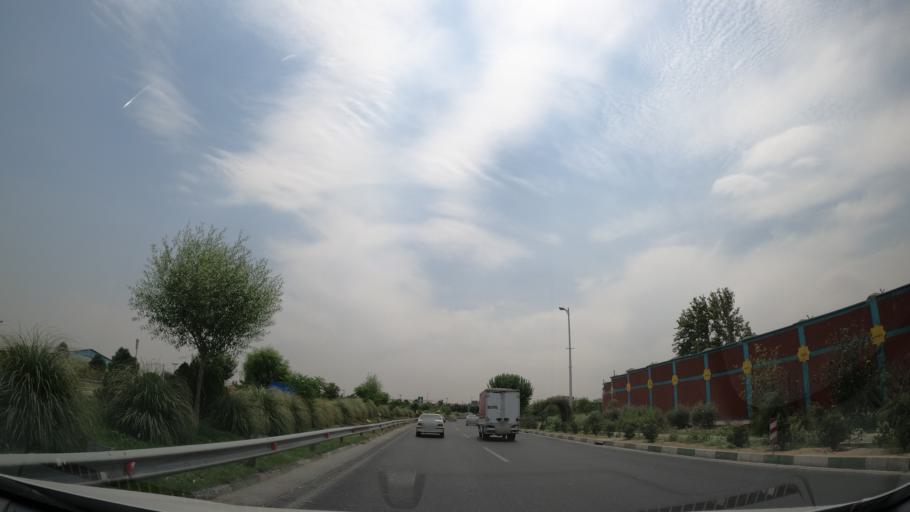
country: IR
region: Tehran
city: Tehran
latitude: 35.6834
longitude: 51.3424
